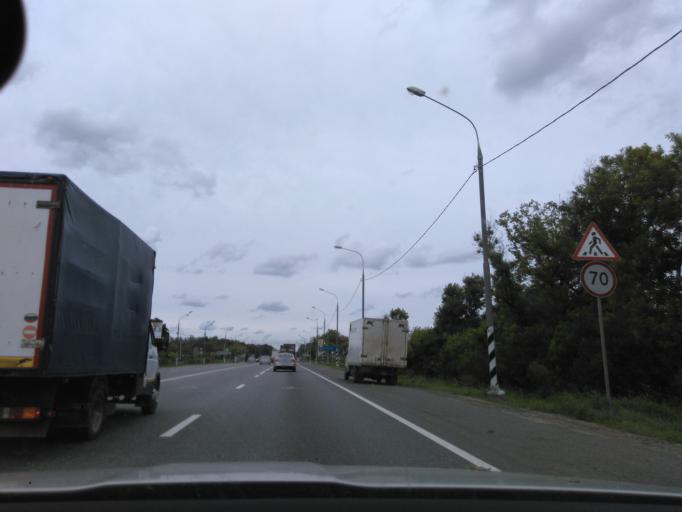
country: RU
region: Moskovskaya
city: Klin
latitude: 56.3057
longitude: 36.7865
